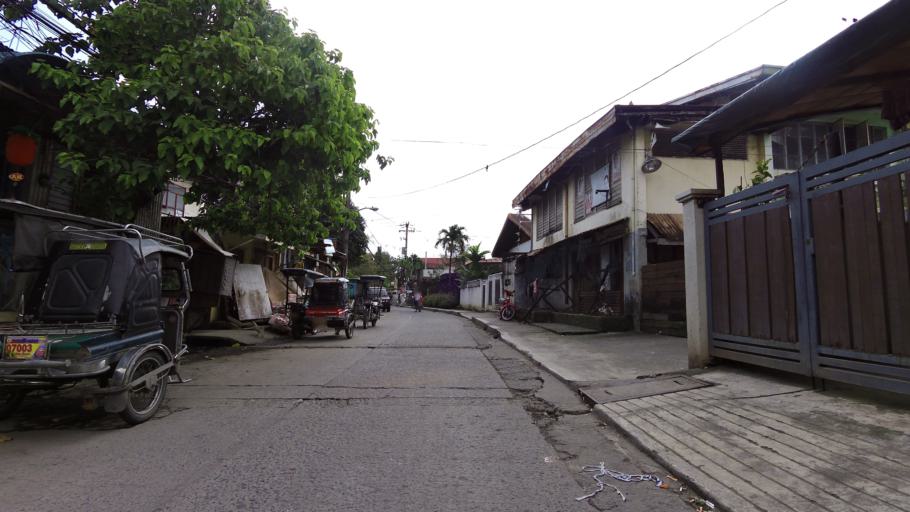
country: PH
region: Calabarzon
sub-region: Province of Rizal
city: Cainta
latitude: 14.5707
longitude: 121.1246
